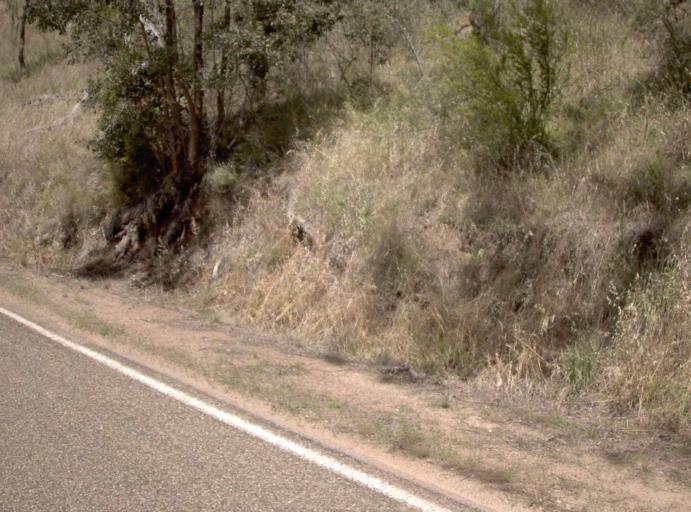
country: AU
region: Victoria
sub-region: East Gippsland
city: Bairnsdale
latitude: -37.3896
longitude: 147.8285
